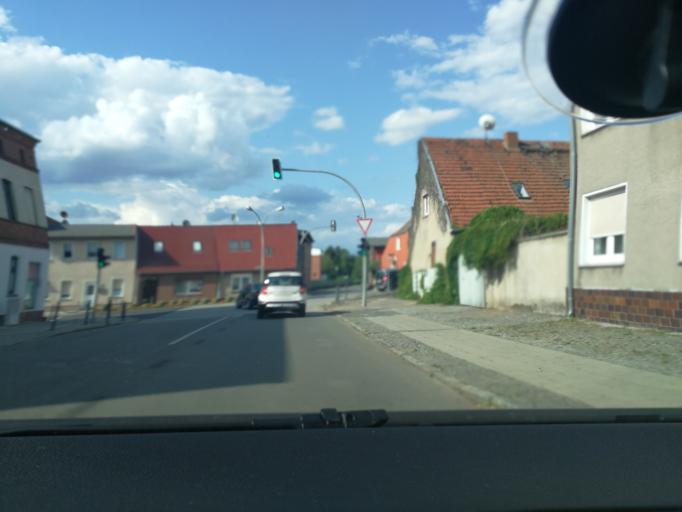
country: DE
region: Brandenburg
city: Pritzwalk
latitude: 53.1499
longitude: 12.1847
